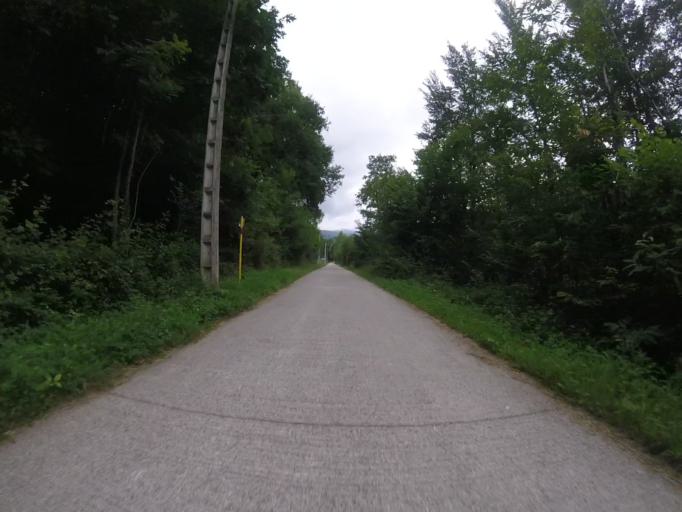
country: ES
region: Navarre
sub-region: Provincia de Navarra
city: Sunbilla
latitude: 43.1522
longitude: -1.6693
